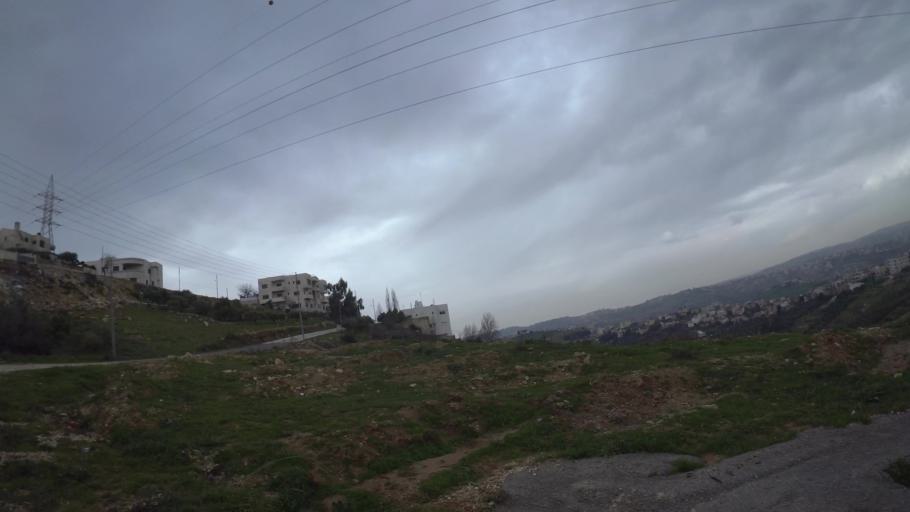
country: JO
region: Amman
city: Umm as Summaq
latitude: 31.9087
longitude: 35.8339
